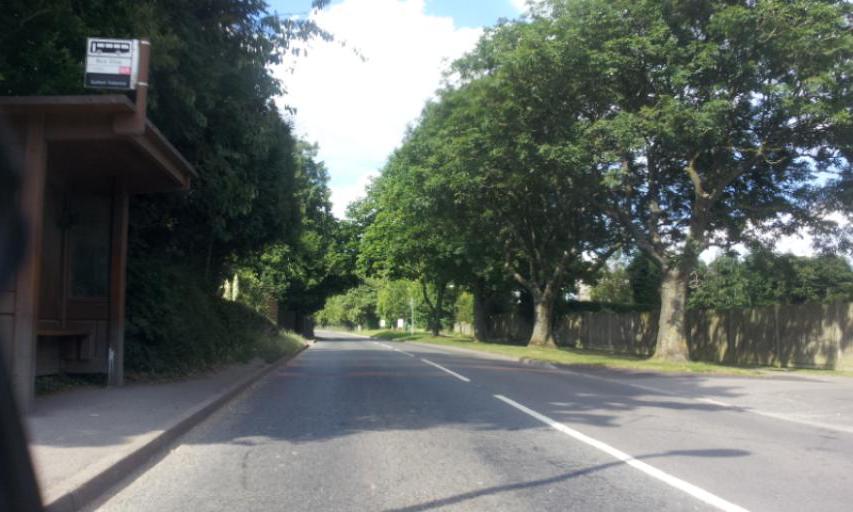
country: GB
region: England
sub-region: Kent
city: Headcorn
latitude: 51.2154
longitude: 0.5918
